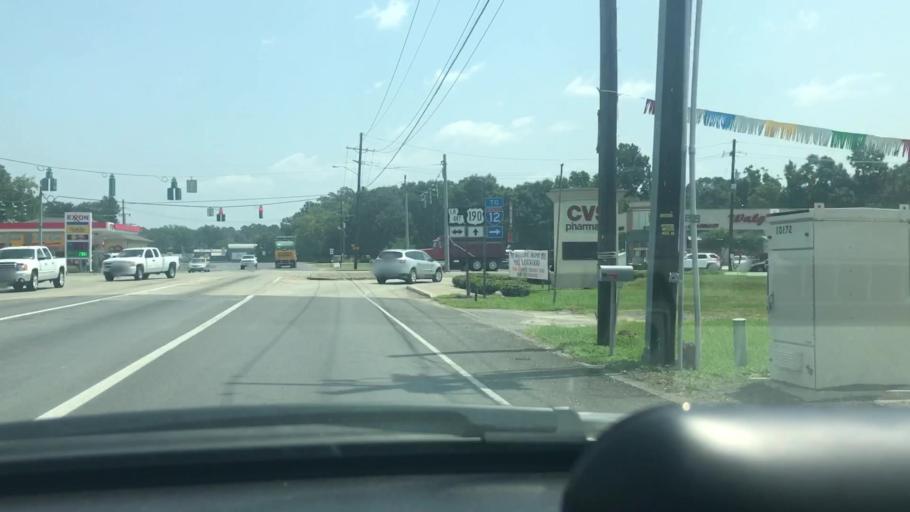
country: US
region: Louisiana
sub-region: Livingston Parish
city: Walker
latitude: 30.4880
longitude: -90.8624
